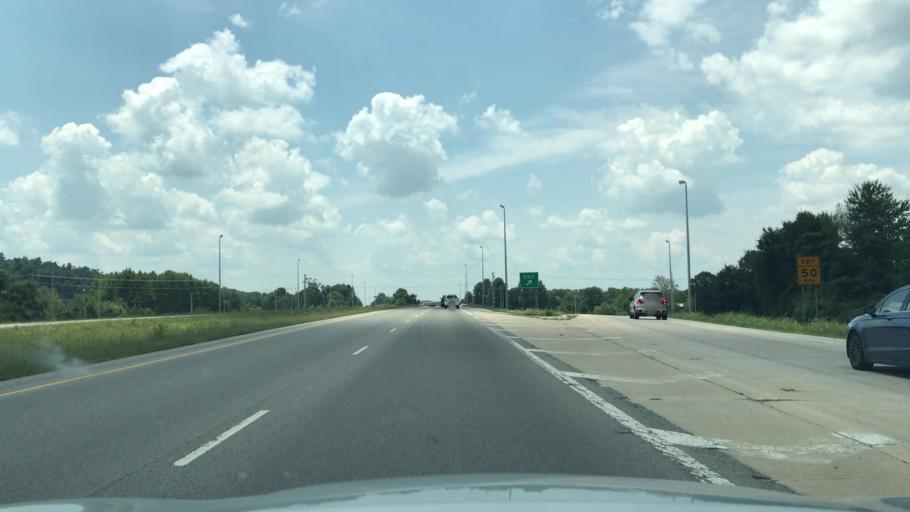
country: US
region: Tennessee
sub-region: Putnam County
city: Cookeville
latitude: 36.1546
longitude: -85.4725
